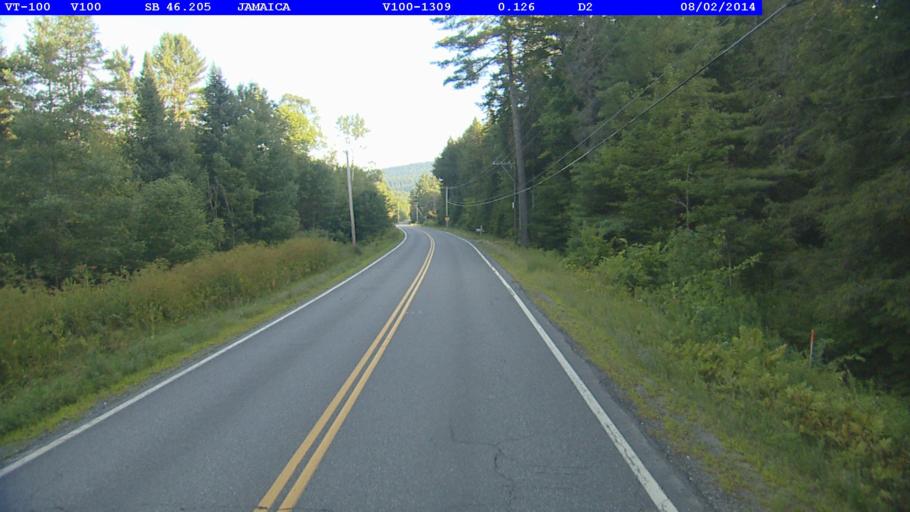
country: US
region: Vermont
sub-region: Windham County
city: Dover
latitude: 43.0534
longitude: -72.7854
